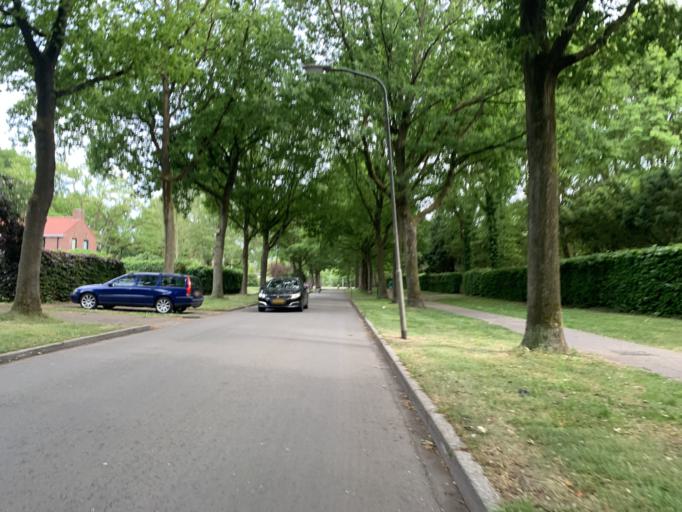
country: NL
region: Groningen
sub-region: Gemeente Haren
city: Haren
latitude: 53.1639
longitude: 6.6160
